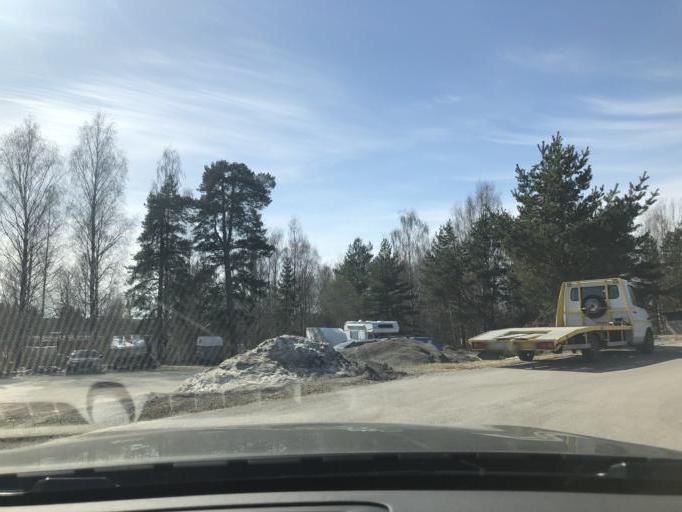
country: SE
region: Gaevleborg
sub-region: Hudiksvalls Kommun
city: Hudiksvall
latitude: 61.7237
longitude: 17.1464
